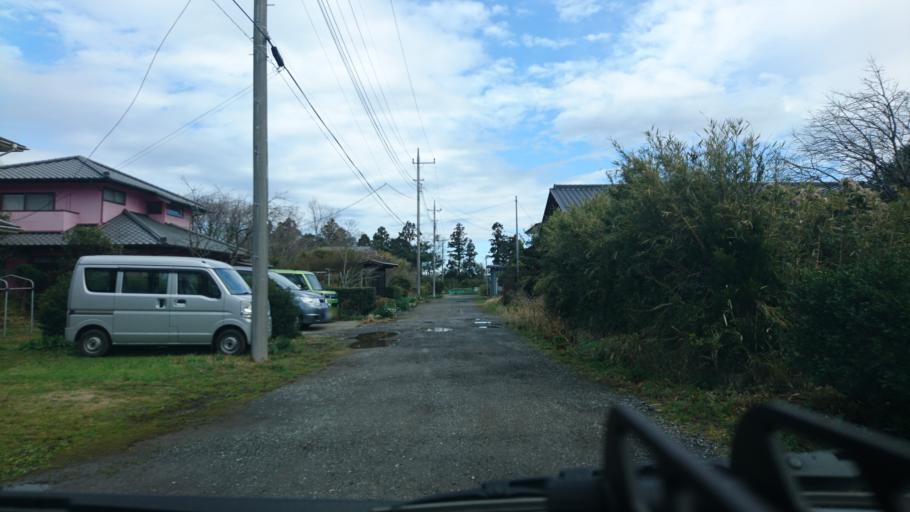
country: JP
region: Chiba
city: Kimitsu
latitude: 35.2932
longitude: 139.9665
